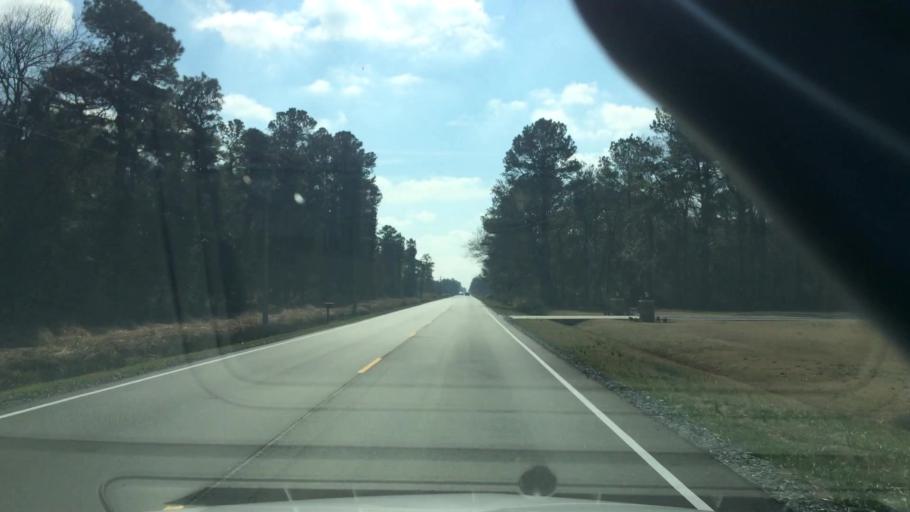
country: US
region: North Carolina
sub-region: Duplin County
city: Beulaville
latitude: 35.0254
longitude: -77.7491
